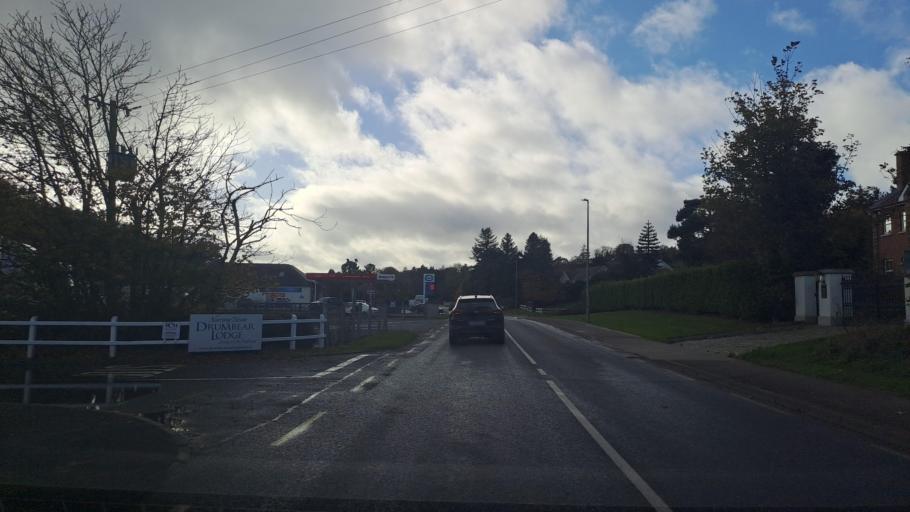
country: IE
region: Ulster
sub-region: County Monaghan
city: Monaghan
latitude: 54.2290
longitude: -6.9698
